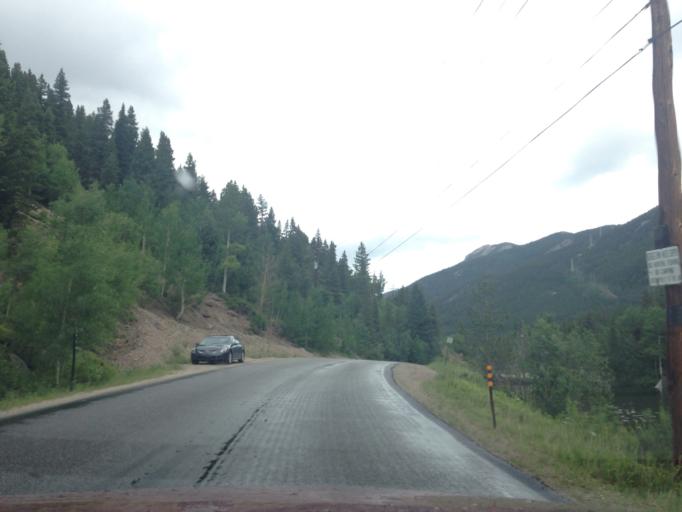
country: US
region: Colorado
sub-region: Clear Creek County
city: Georgetown
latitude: 39.6915
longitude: -105.6984
